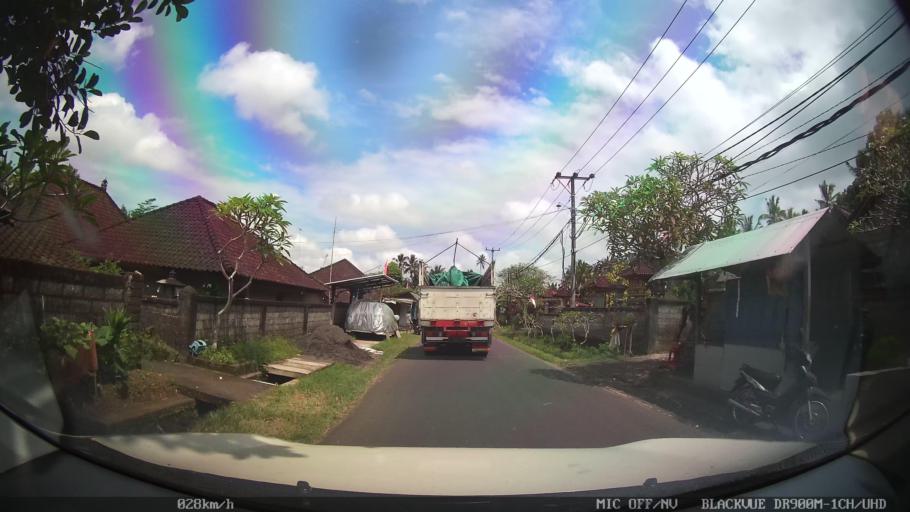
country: ID
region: Bali
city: Banjar Kelodan
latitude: -8.4842
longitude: 115.3677
